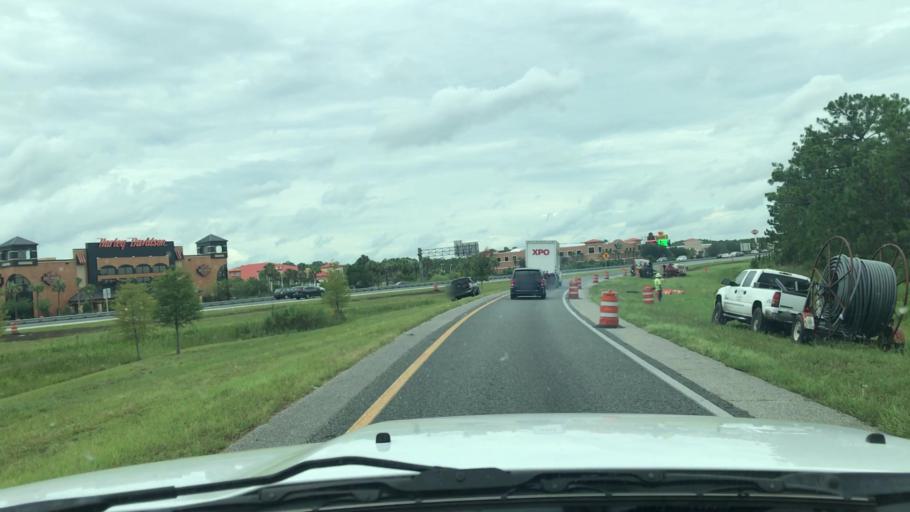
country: US
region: Florida
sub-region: Volusia County
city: Ormond-by-the-Sea
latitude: 29.3383
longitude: -81.1300
